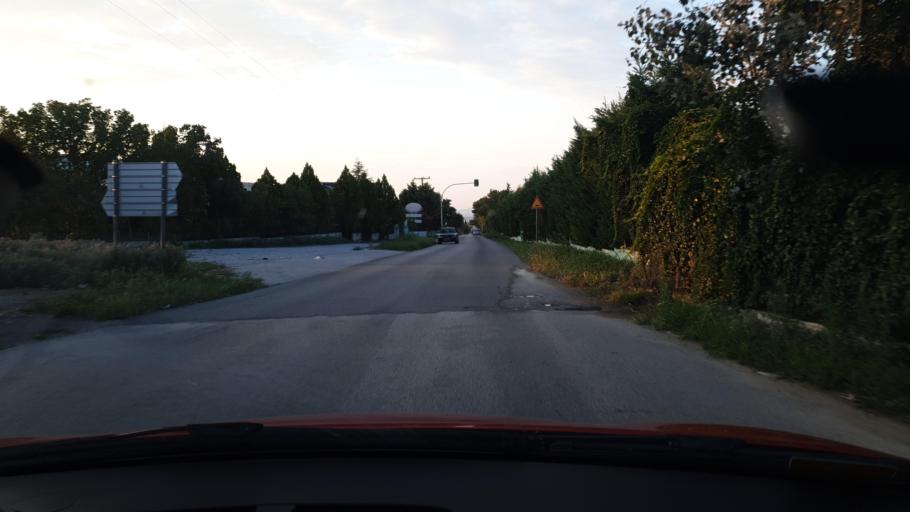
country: GR
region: Central Macedonia
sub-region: Nomos Thessalonikis
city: Peraia
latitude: 40.5014
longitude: 22.9501
